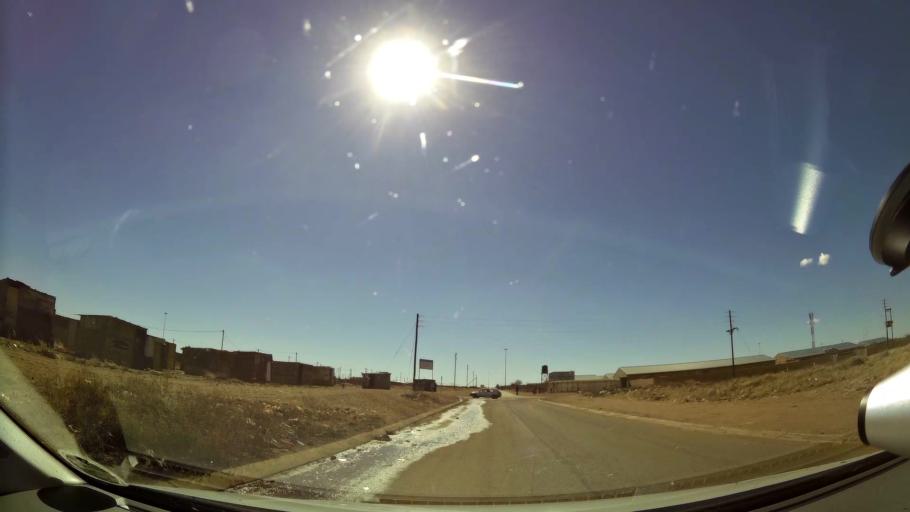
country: ZA
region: North-West
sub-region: Dr Kenneth Kaunda District Municipality
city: Klerksdorp
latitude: -26.8737
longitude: 26.5644
